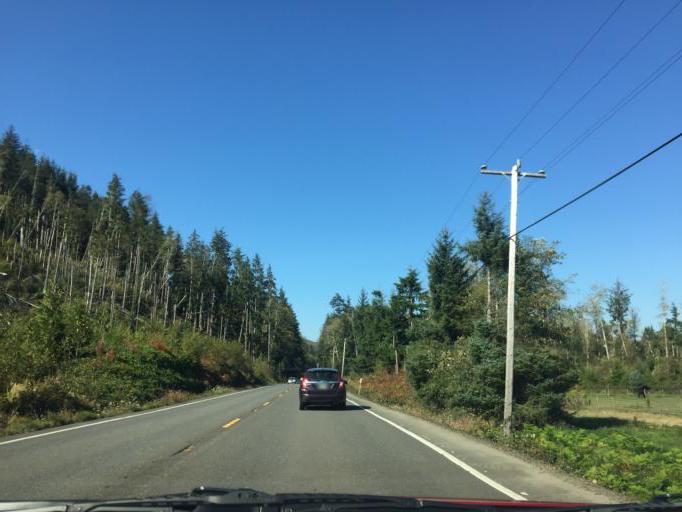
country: US
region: Oregon
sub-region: Clatsop County
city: Cannon Beach
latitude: 45.9031
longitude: -123.8724
